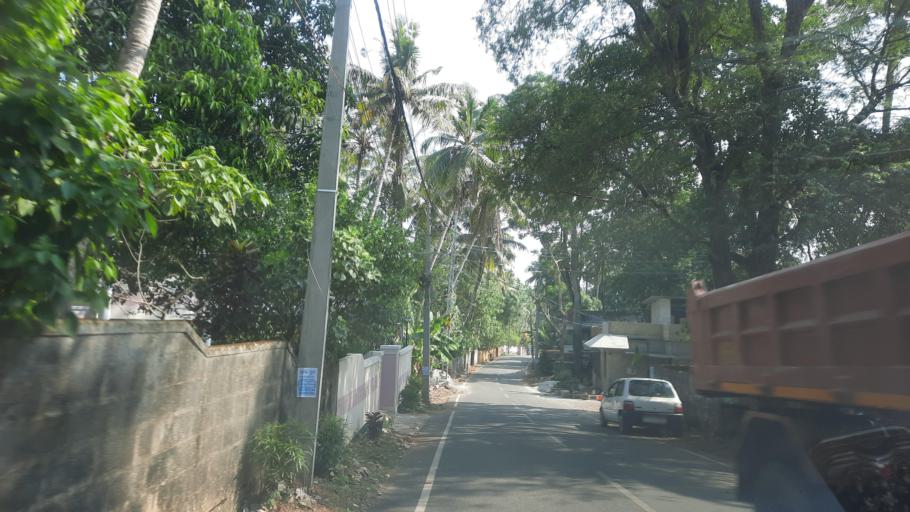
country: IN
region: Kerala
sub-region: Thiruvananthapuram
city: Nedumangad
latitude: 8.5877
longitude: 76.9319
